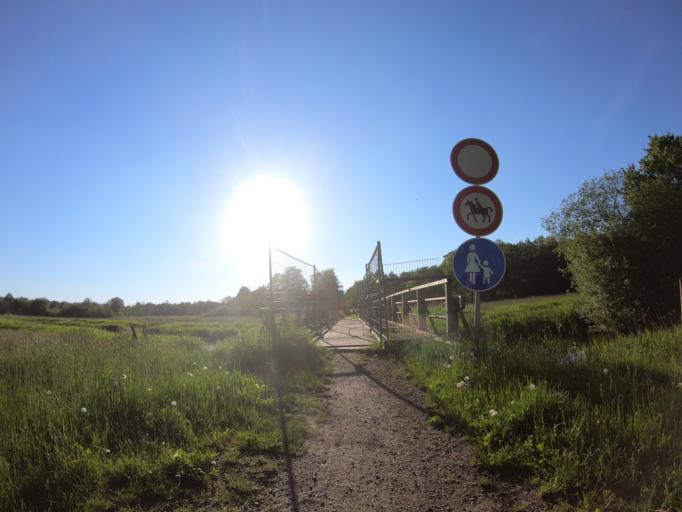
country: DE
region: Lower Saxony
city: Wagenhoff
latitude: 52.5467
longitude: 10.5615
